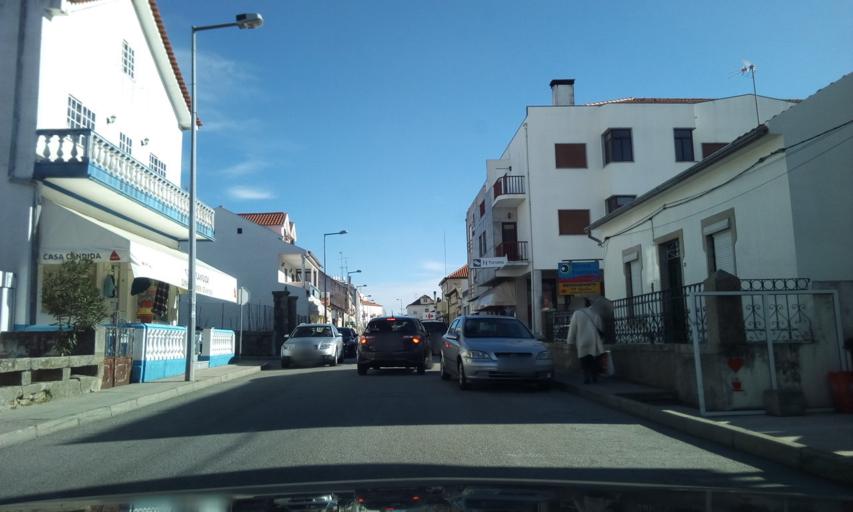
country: ES
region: Castille and Leon
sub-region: Provincia de Salamanca
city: Fuentes de Onoro
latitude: 40.6087
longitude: -6.8301
